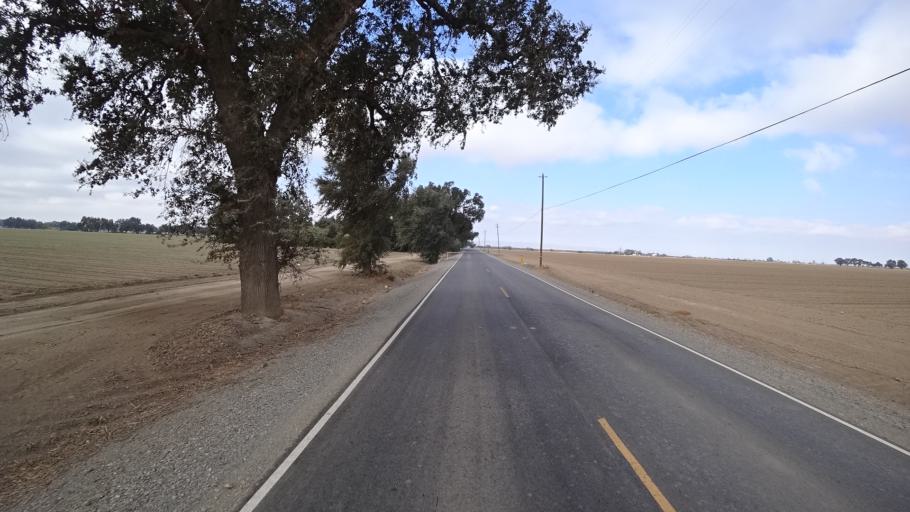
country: US
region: California
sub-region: Yolo County
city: Woodland
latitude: 38.7937
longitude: -121.8326
